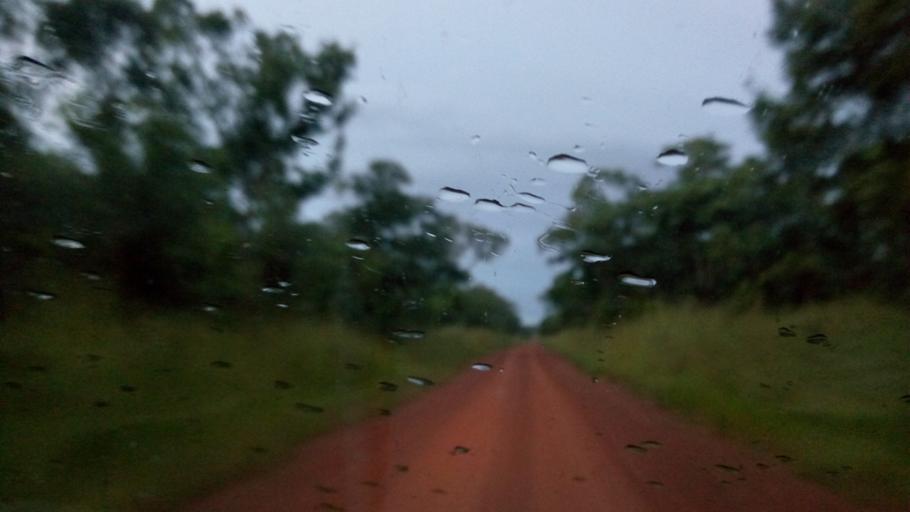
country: ZM
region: Luapula
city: Mwense
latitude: -9.8488
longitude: 28.1233
